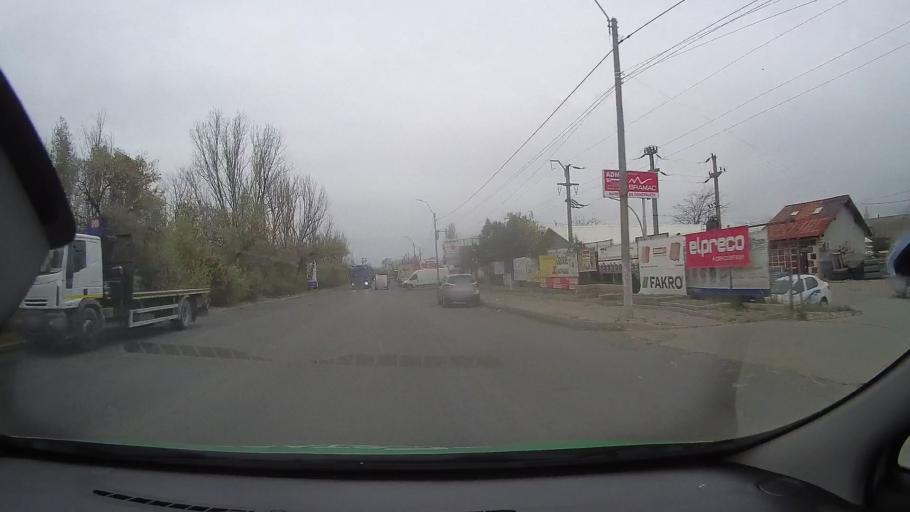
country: RO
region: Ialomita
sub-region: Comuna Slobozia
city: Slobozia
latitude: 44.5752
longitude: 27.3862
